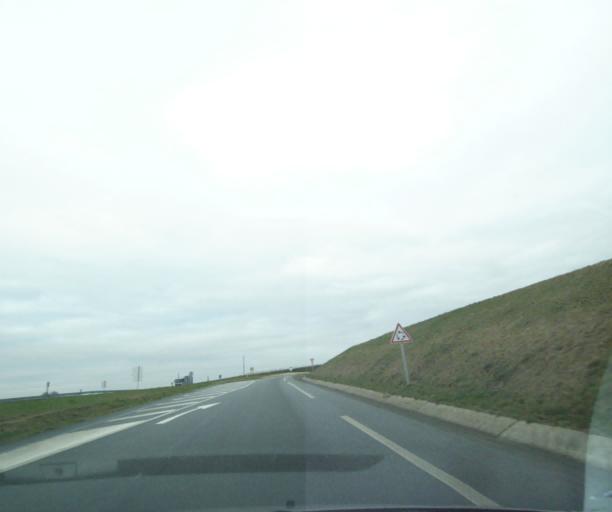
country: FR
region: Picardie
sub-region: Departement de l'Oise
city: Noyon
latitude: 49.5679
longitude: 2.9742
